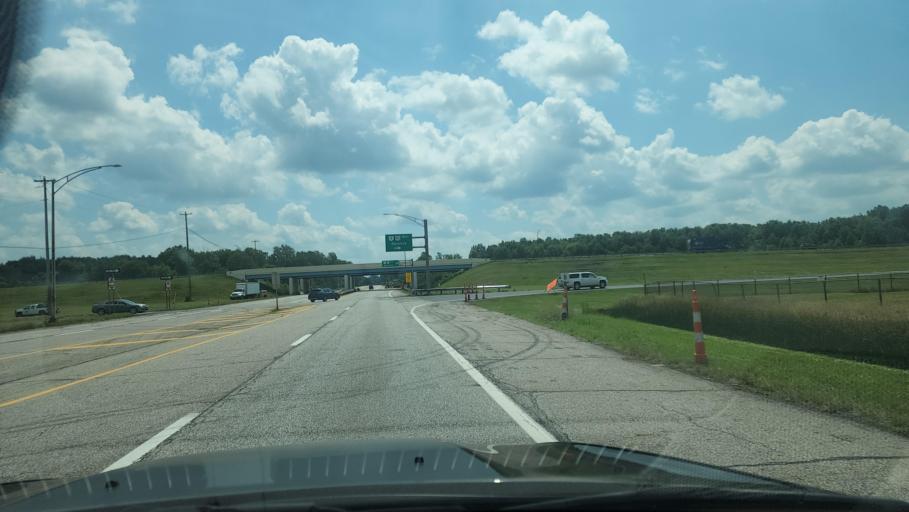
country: US
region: Ohio
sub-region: Trumbull County
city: Leavittsburg
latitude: 41.2640
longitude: -80.8783
